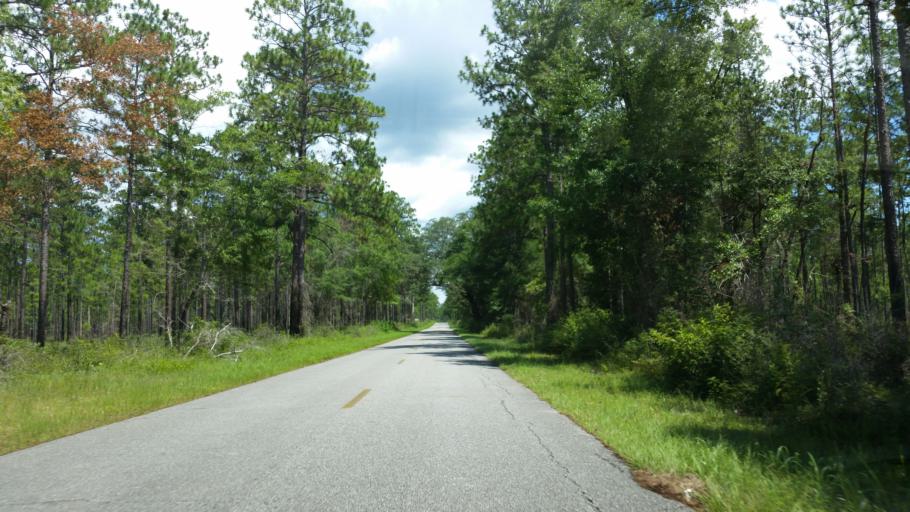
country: US
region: Florida
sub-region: Okaloosa County
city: Crestview
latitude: 30.7315
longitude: -86.8060
